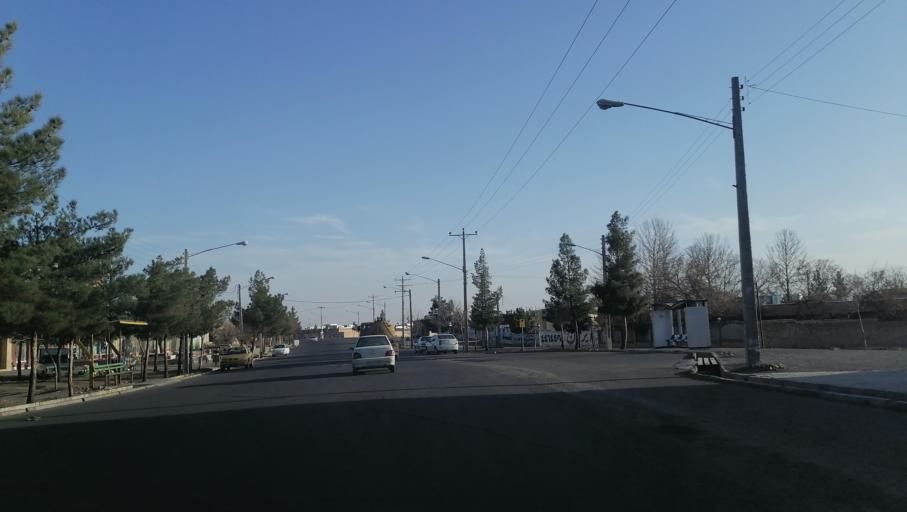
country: IR
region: Razavi Khorasan
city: Sabzevar
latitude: 36.2782
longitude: 57.6757
